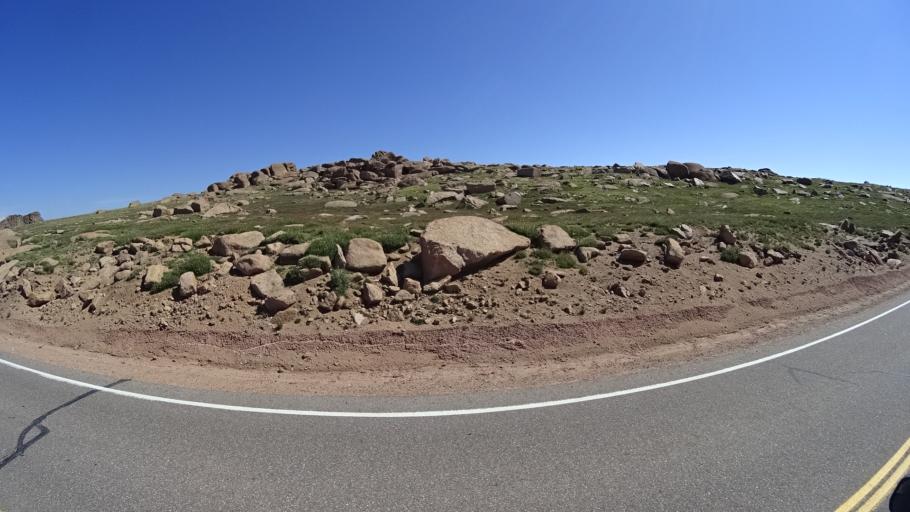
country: US
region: Colorado
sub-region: El Paso County
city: Cascade-Chipita Park
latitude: 38.8521
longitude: -105.0626
